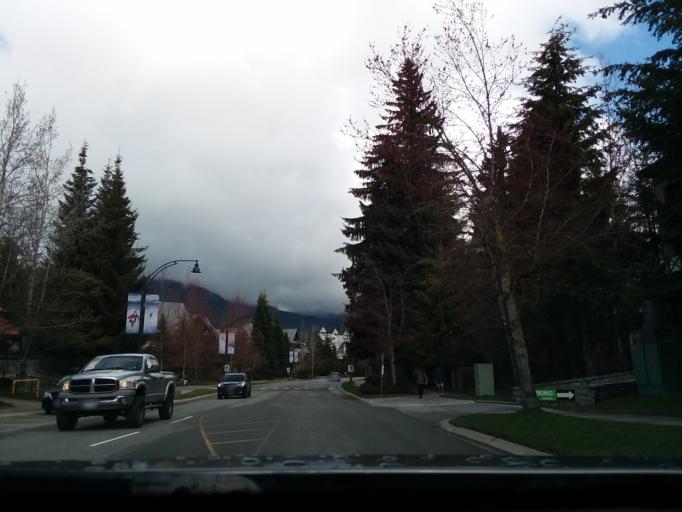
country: CA
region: British Columbia
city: Whistler
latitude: 50.1174
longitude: -122.9579
